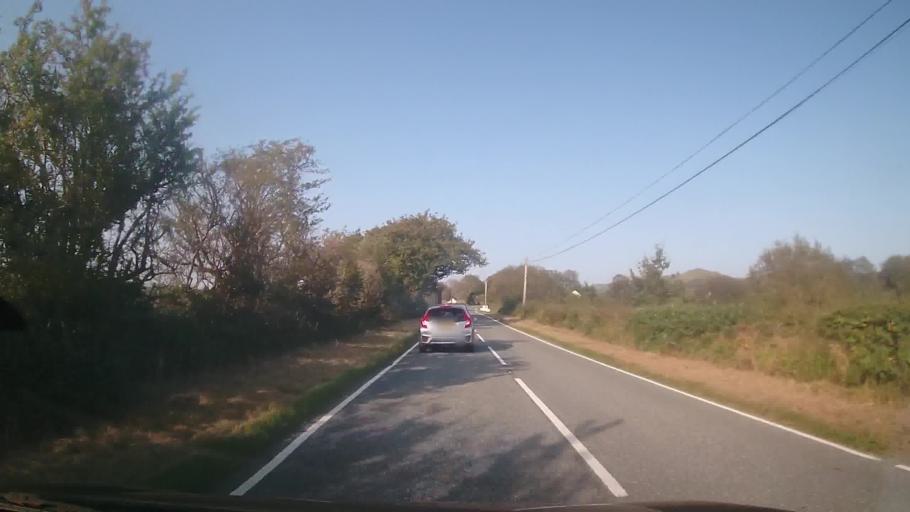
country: GB
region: Wales
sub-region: County of Ceredigion
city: Lledrod
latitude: 52.2753
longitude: -3.8682
